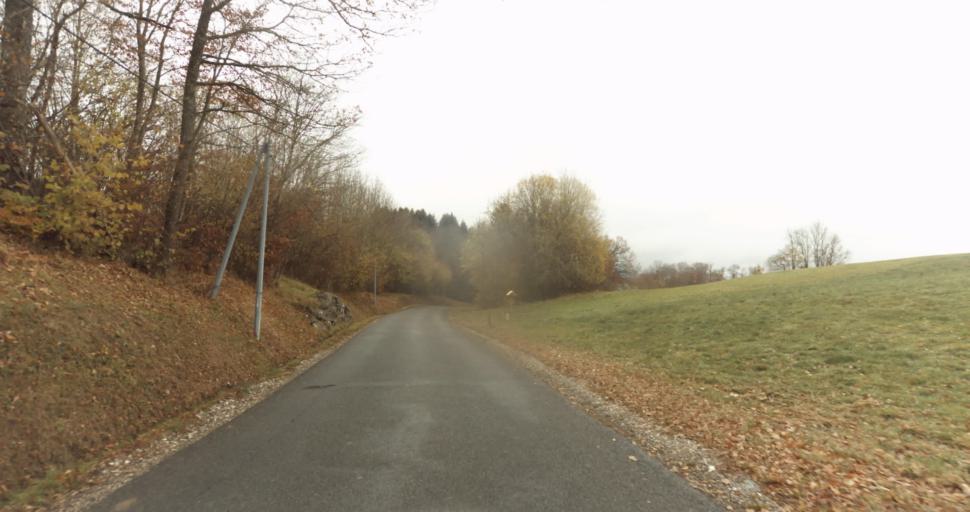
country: FR
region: Rhone-Alpes
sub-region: Departement de la Haute-Savoie
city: Evires
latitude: 46.0561
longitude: 6.2087
